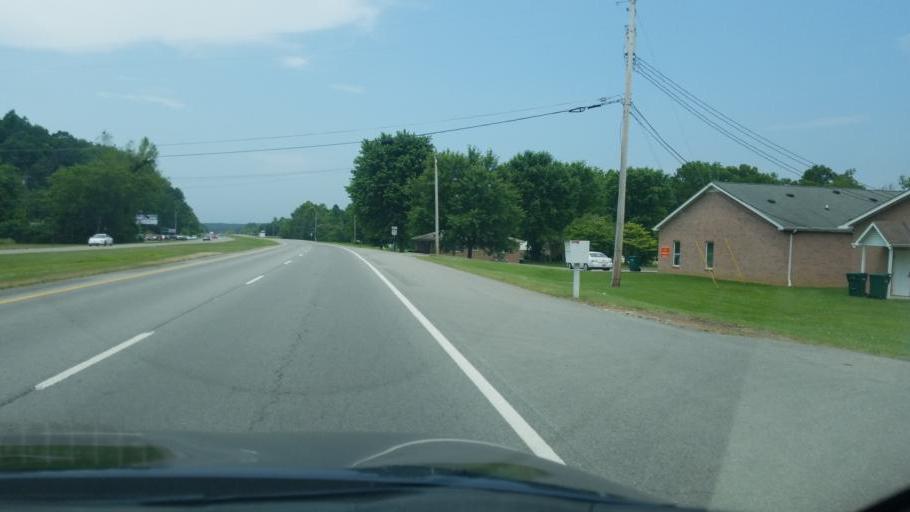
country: US
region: Tennessee
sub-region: Humphreys County
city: Waverly
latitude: 36.0793
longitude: -87.8411
